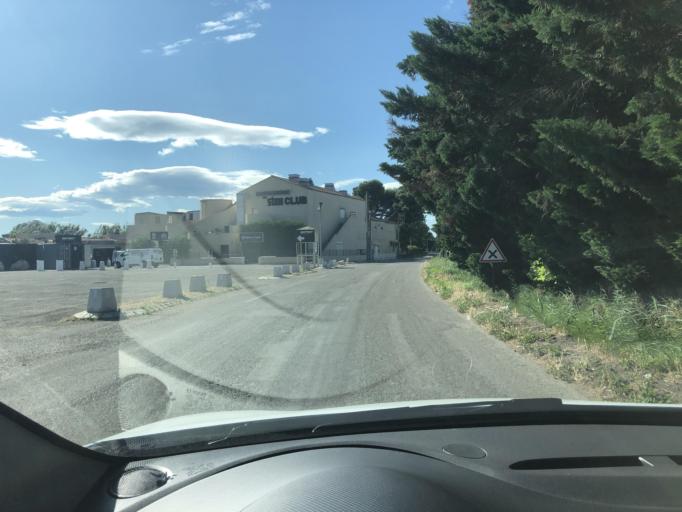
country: FR
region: Provence-Alpes-Cote d'Azur
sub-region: Departement des Bouches-du-Rhone
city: Rognonas
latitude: 43.9039
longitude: 4.8302
